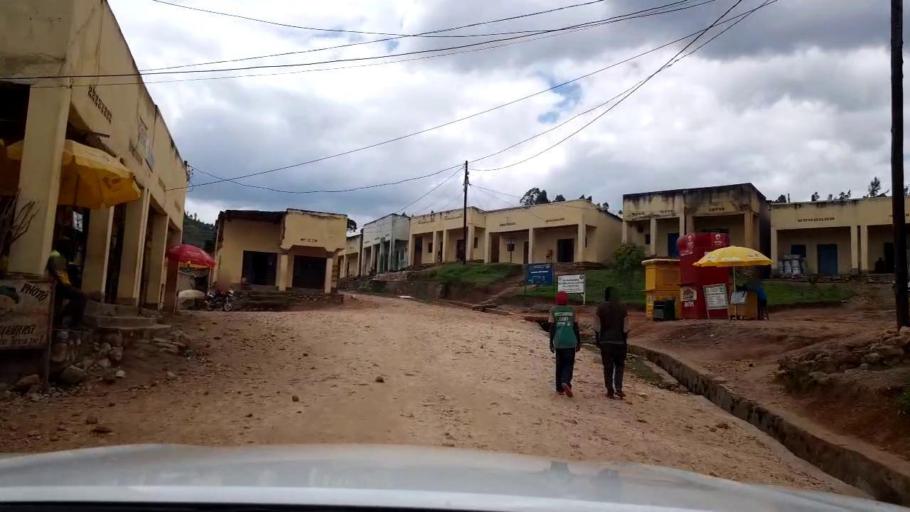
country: RW
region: Southern Province
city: Gitarama
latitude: -1.9414
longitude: 29.6271
